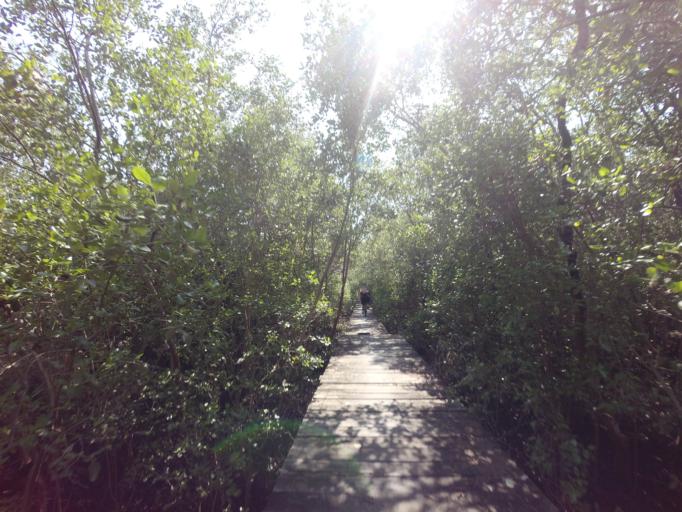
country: TH
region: Bangkok
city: Thung Khru
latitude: 13.5022
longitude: 100.4235
